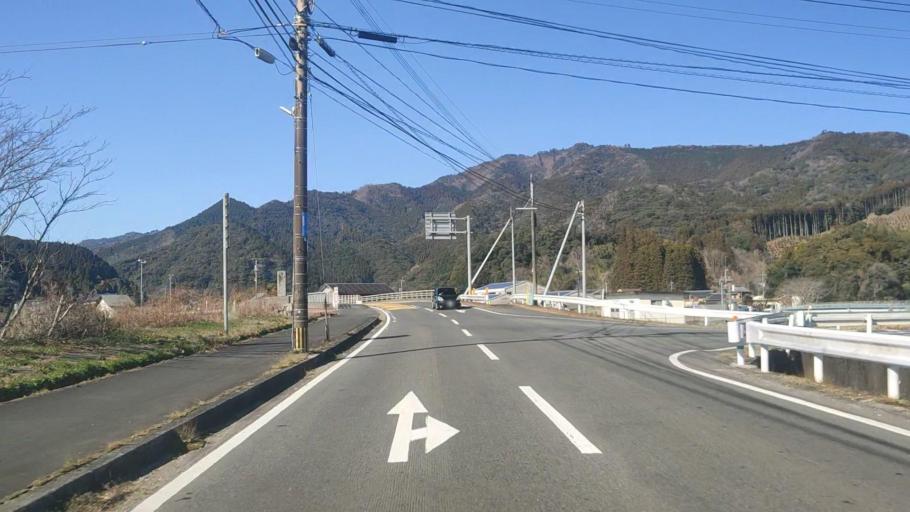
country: JP
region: Oita
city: Saiki
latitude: 32.9780
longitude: 131.8511
